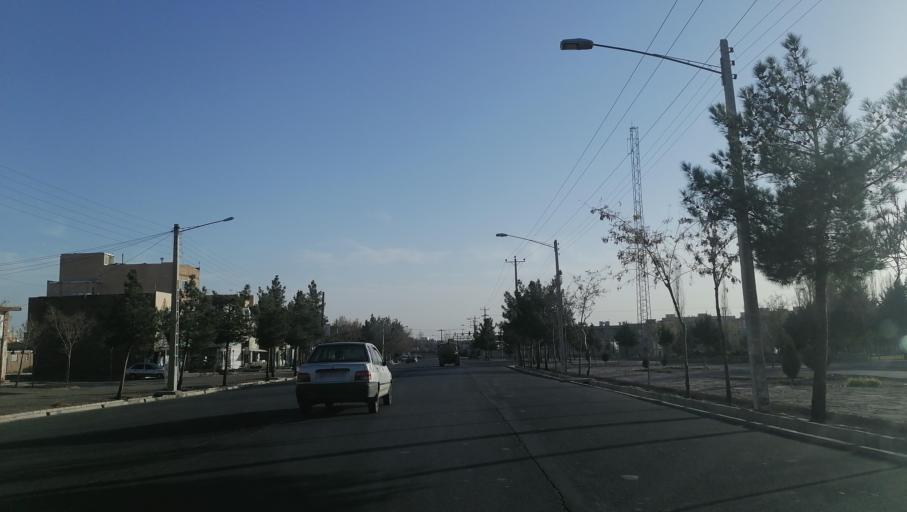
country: IR
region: Razavi Khorasan
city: Sabzevar
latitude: 36.2804
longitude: 57.6753
